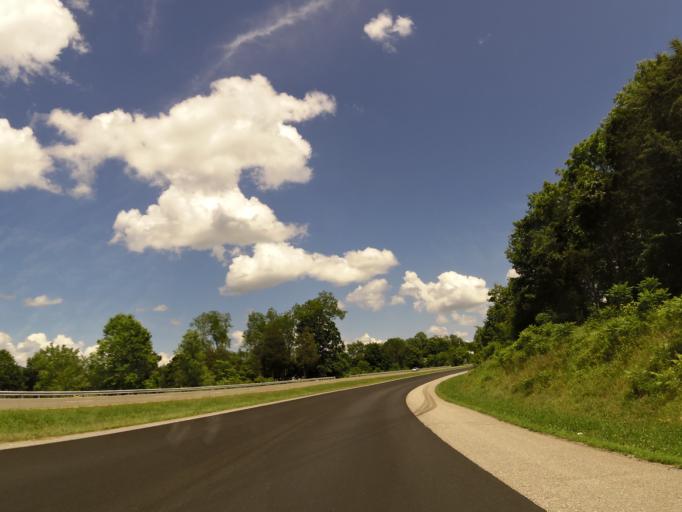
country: US
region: Virginia
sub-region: Lee County
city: Jonesville
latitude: 36.6990
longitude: -83.2575
